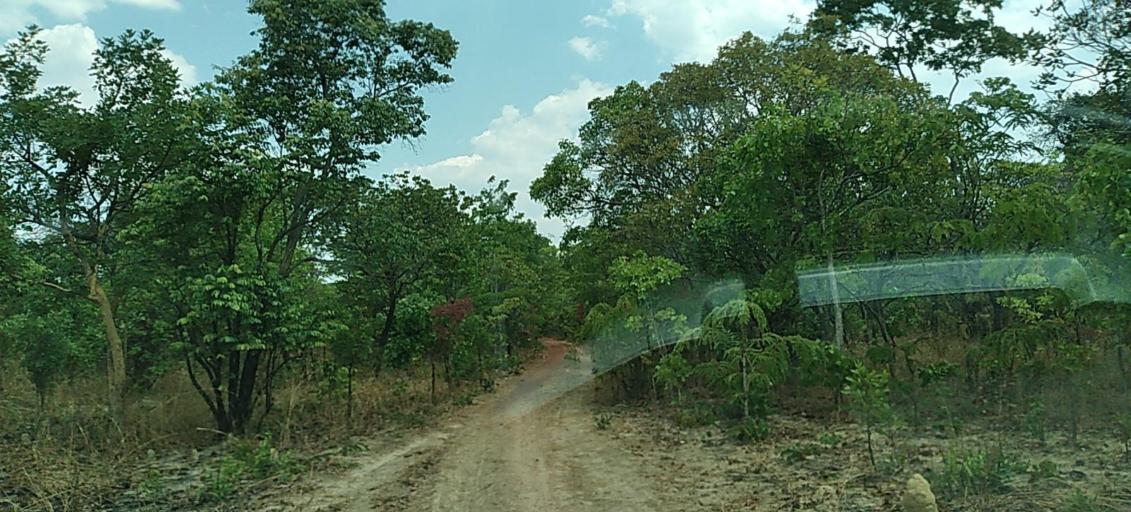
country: CD
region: Katanga
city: Kipushi
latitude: -11.9806
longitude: 27.4156
